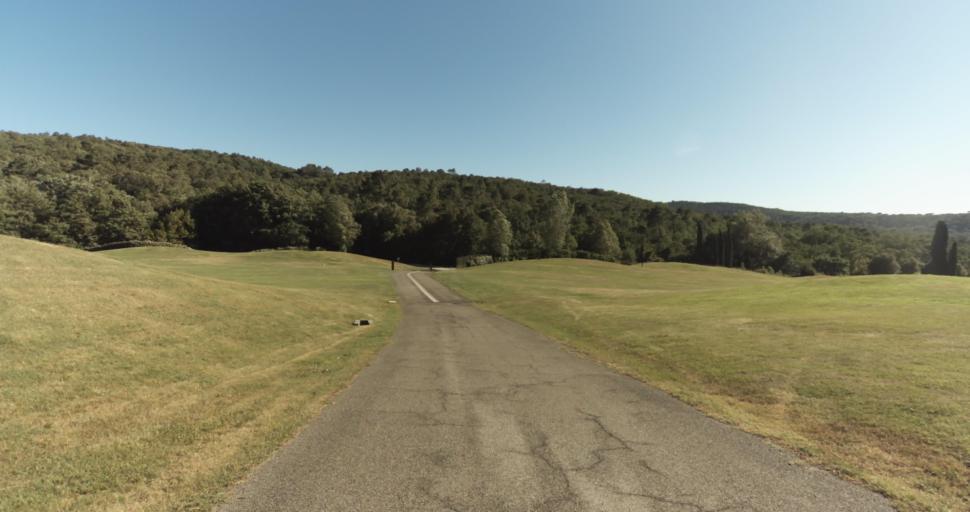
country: FR
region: Provence-Alpes-Cote d'Azur
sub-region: Departement du Var
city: Gassin
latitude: 43.2526
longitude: 6.6063
